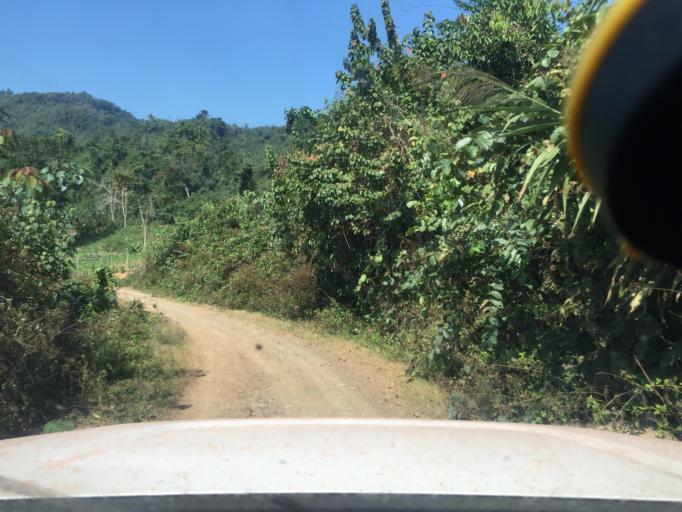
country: LA
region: Phongsali
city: Phongsali
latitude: 21.6585
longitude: 102.4209
